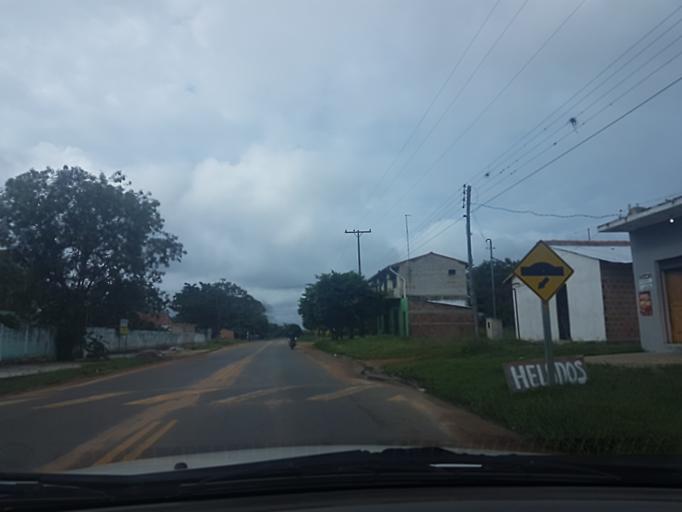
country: PY
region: Central
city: Limpio
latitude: -25.2189
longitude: -57.4473
